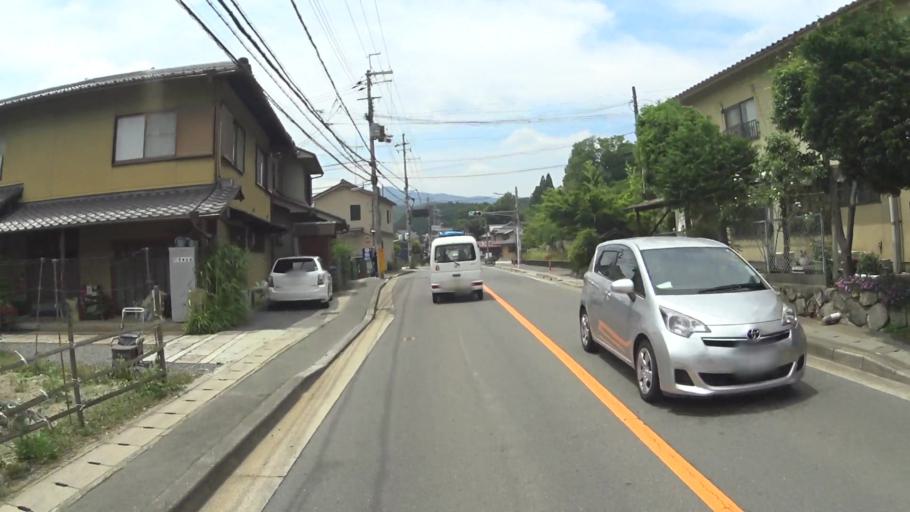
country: JP
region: Kyoto
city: Kyoto
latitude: 35.0352
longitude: 135.6973
